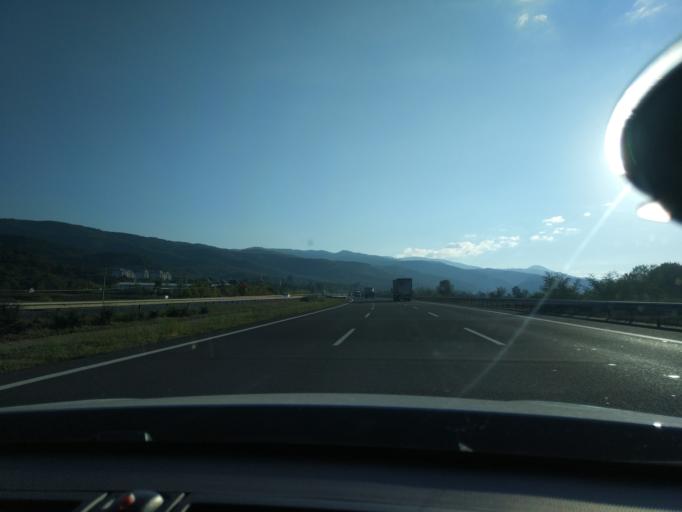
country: TR
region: Duzce
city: Kaynasli
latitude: 40.7800
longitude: 31.3280
